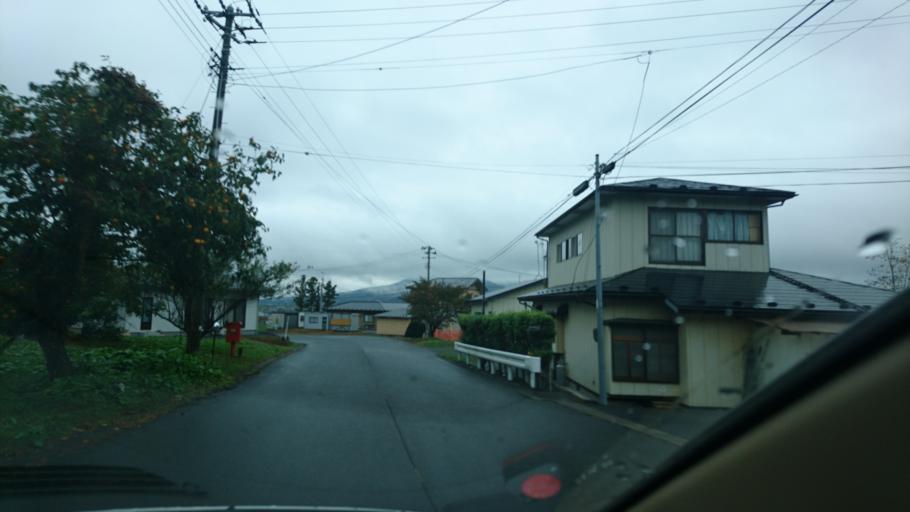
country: JP
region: Iwate
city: Ichinoseki
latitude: 38.9713
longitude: 141.1090
